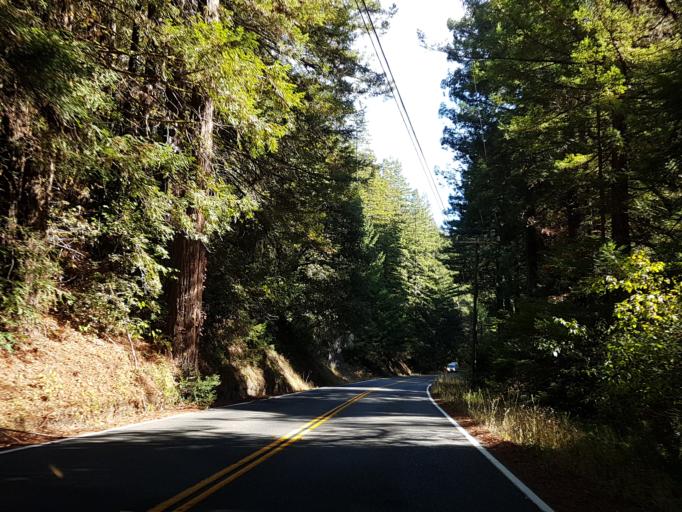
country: US
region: California
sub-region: Humboldt County
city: Rio Dell
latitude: 40.4100
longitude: -123.9559
